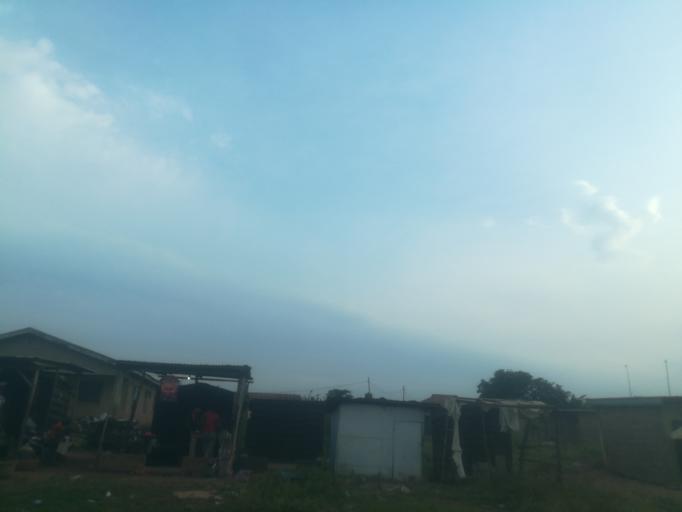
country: NG
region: Ogun
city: Abeokuta
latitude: 7.1405
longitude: 3.2676
